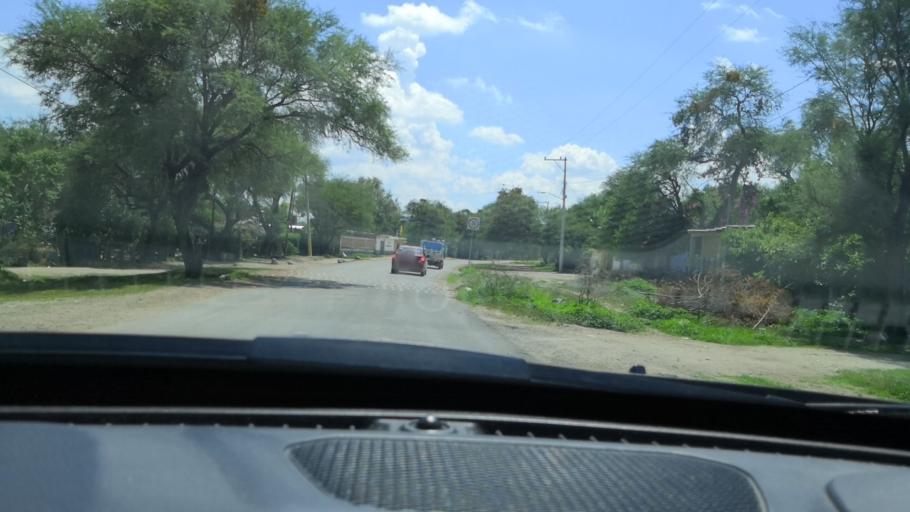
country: MX
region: Guanajuato
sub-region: Leon
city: Plan Guanajuato (La Sandia)
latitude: 20.9373
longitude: -101.6385
